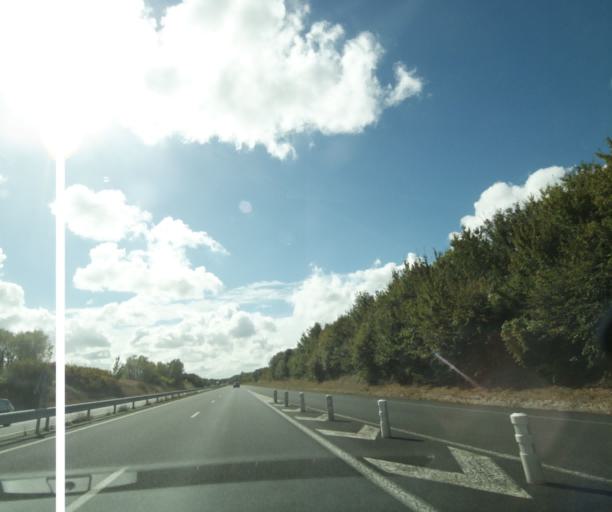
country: FR
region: Poitou-Charentes
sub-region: Departement de la Charente-Maritime
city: Saint-Savinien
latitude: 45.8659
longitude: -0.7324
